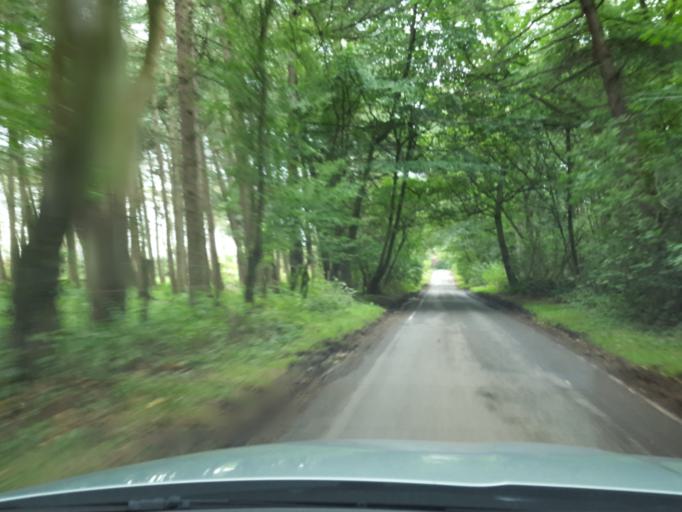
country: GB
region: Scotland
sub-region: West Lothian
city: East Calder
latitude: 55.9144
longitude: -3.4577
